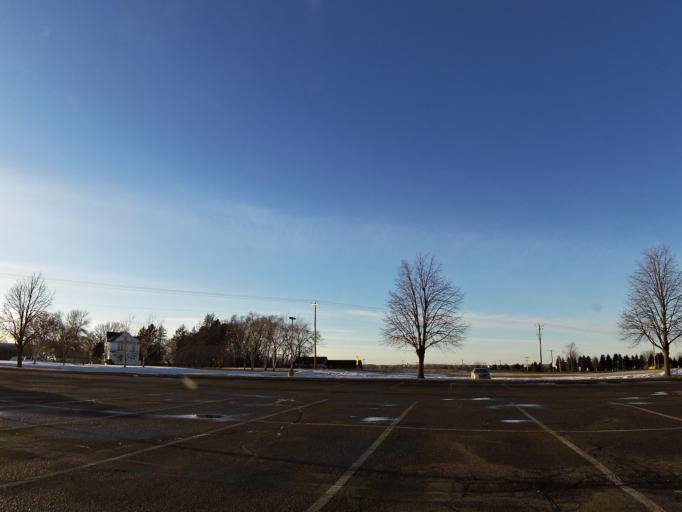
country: US
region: Minnesota
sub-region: Washington County
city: Woodbury
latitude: 44.8887
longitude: -92.9020
